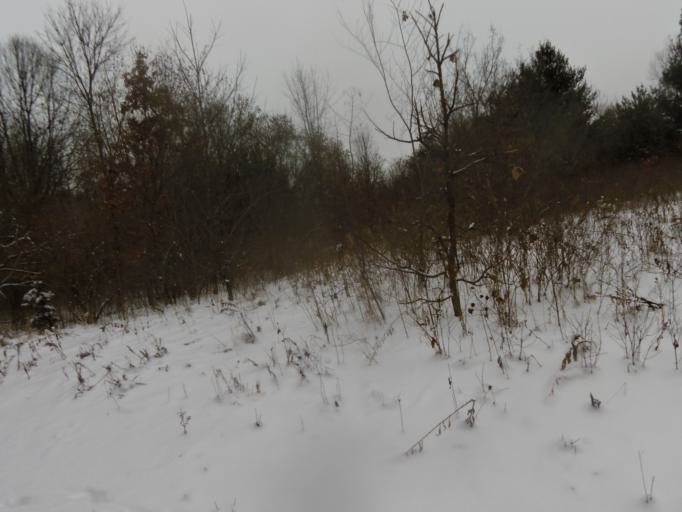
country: US
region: Minnesota
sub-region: Dakota County
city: Inver Grove Heights
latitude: 44.8643
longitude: -93.0751
